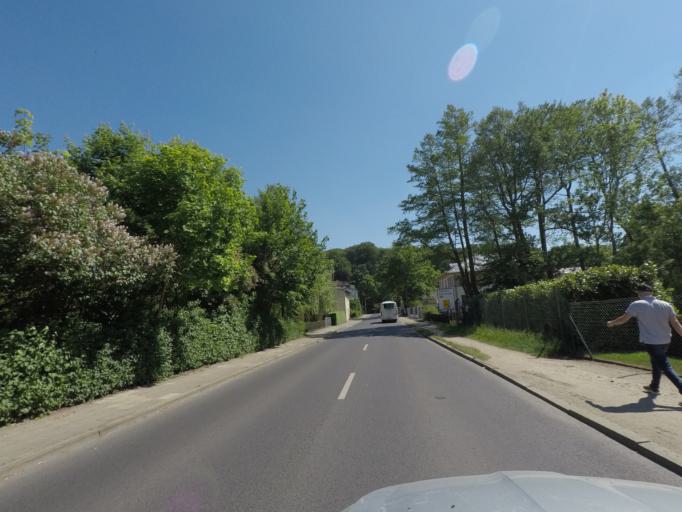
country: DE
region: Brandenburg
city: Eberswalde
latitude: 52.8288
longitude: 13.8078
